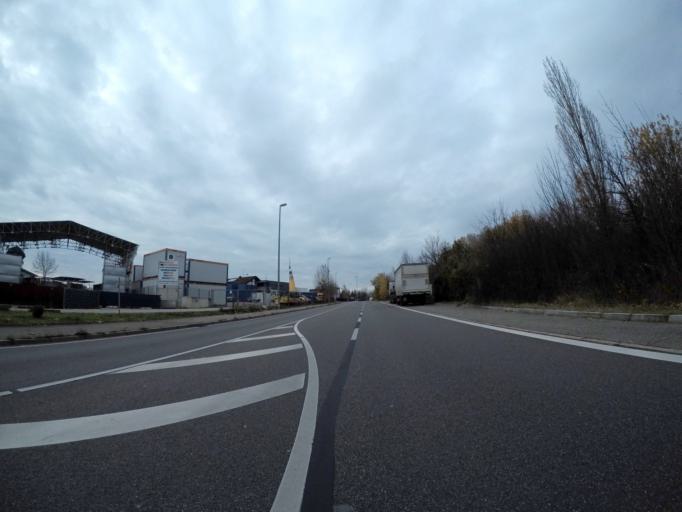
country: DE
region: Baden-Wuerttemberg
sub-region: Tuebingen Region
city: Reutlingen
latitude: 48.5105
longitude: 9.2305
